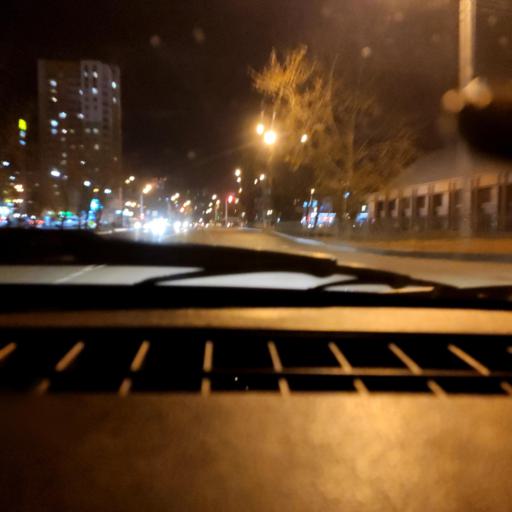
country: RU
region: Bashkortostan
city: Ufa
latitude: 54.7687
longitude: 56.0587
